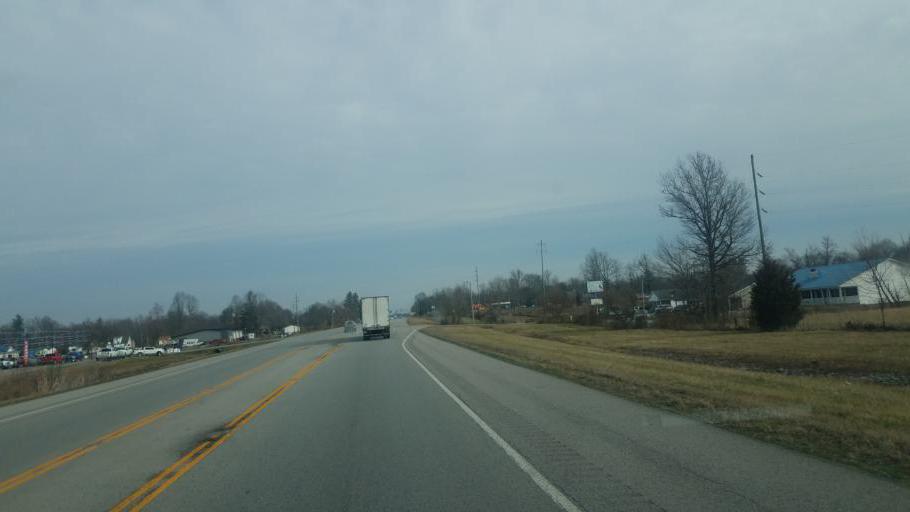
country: US
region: Kentucky
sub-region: Boyle County
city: Junction City
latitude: 37.5785
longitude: -84.7899
